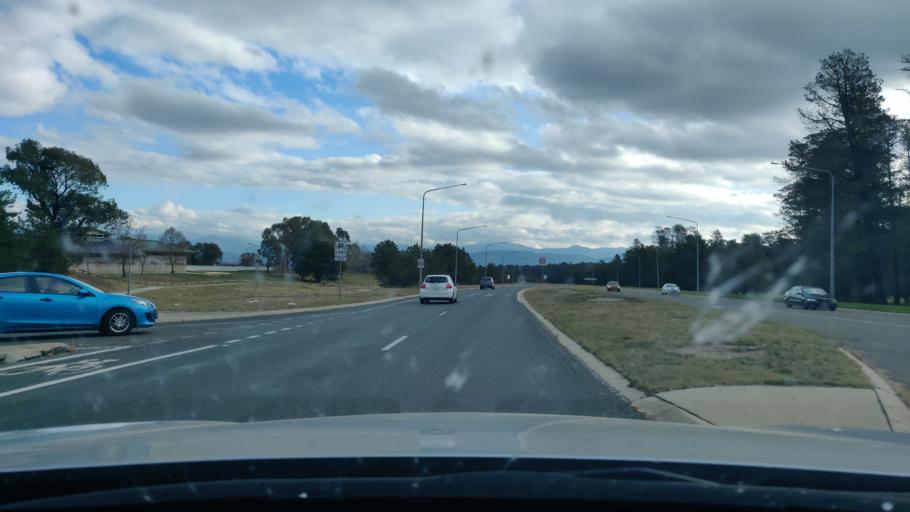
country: AU
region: Australian Capital Territory
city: Macarthur
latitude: -35.4124
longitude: 149.1277
